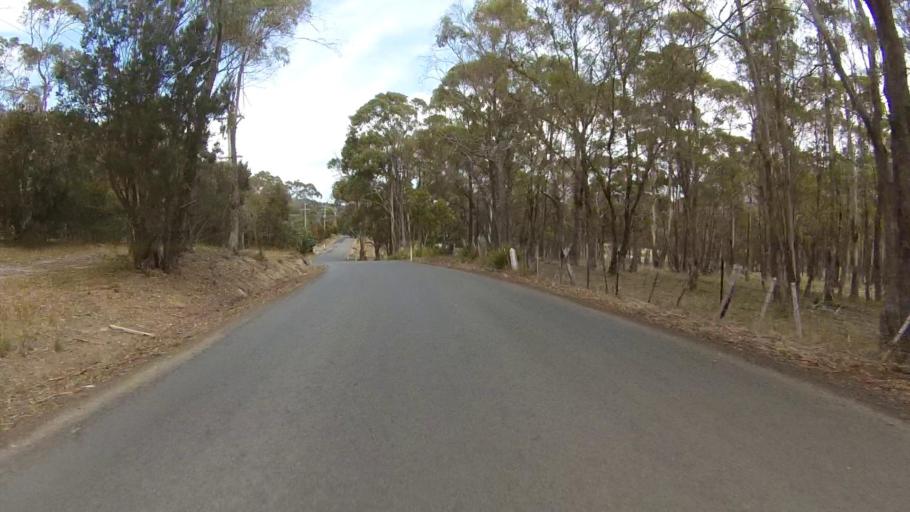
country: AU
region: Tasmania
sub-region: Kingborough
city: Blackmans Bay
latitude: -43.0258
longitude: 147.3131
